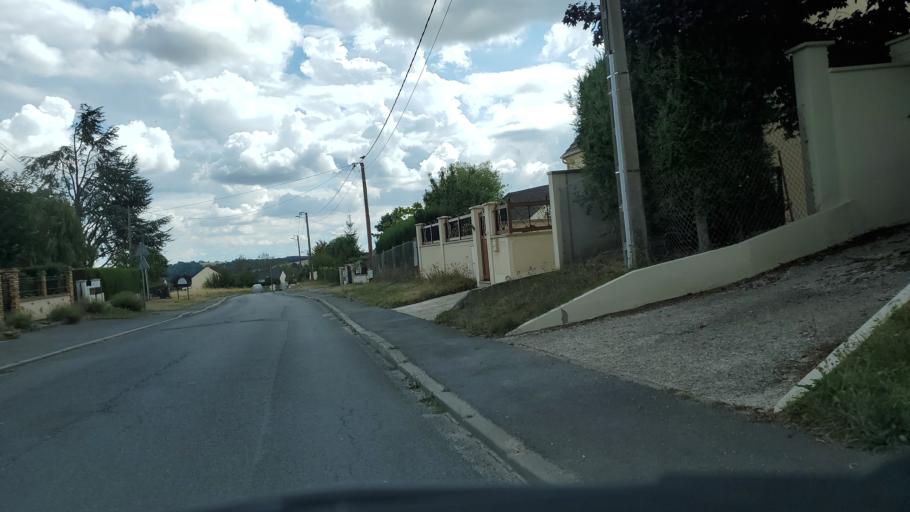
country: FR
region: Ile-de-France
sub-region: Departement de Seine-et-Marne
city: Mouroux
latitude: 48.8301
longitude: 3.0351
